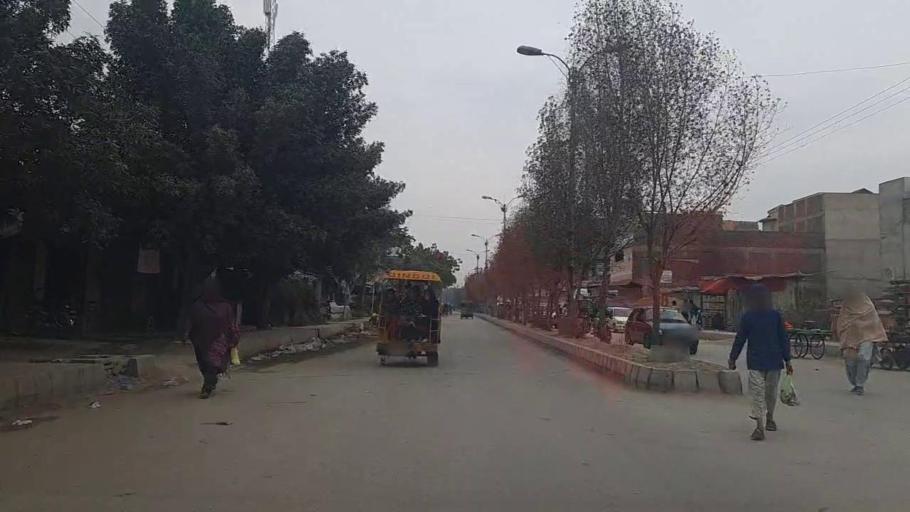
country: PK
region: Sindh
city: Nawabshah
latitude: 26.2564
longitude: 68.4018
